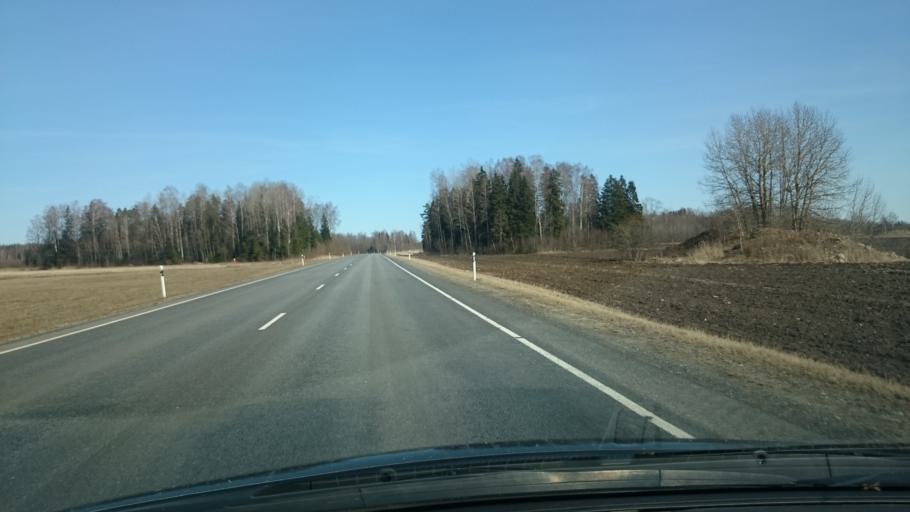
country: EE
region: Paernumaa
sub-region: Vaendra vald (alev)
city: Vandra
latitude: 58.6389
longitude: 24.9641
